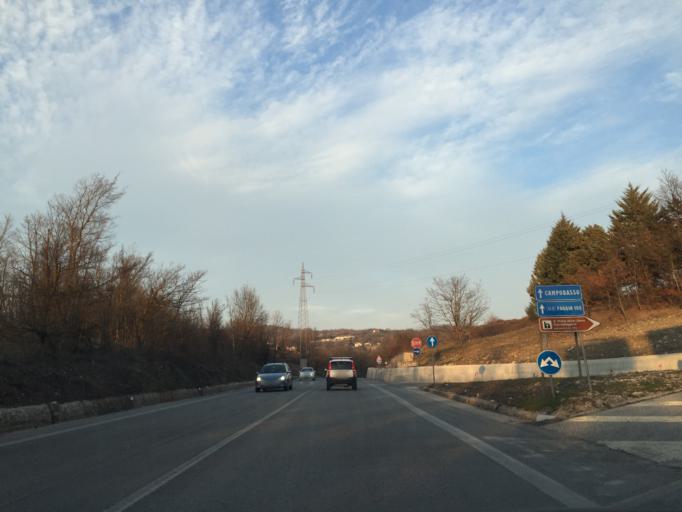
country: IT
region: Molise
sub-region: Provincia di Campobasso
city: Vinchiaturo
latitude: 41.4921
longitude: 14.6030
